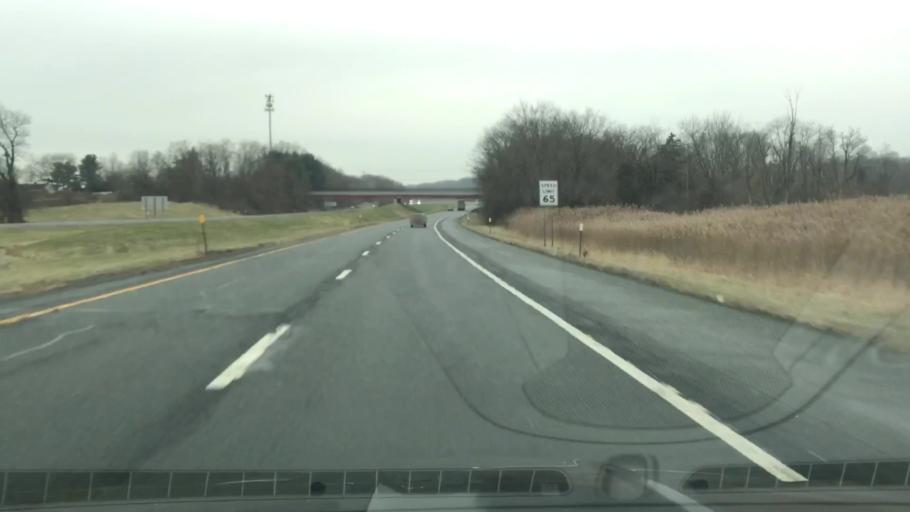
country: US
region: New York
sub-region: Orange County
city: Middletown
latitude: 41.4108
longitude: -74.4373
